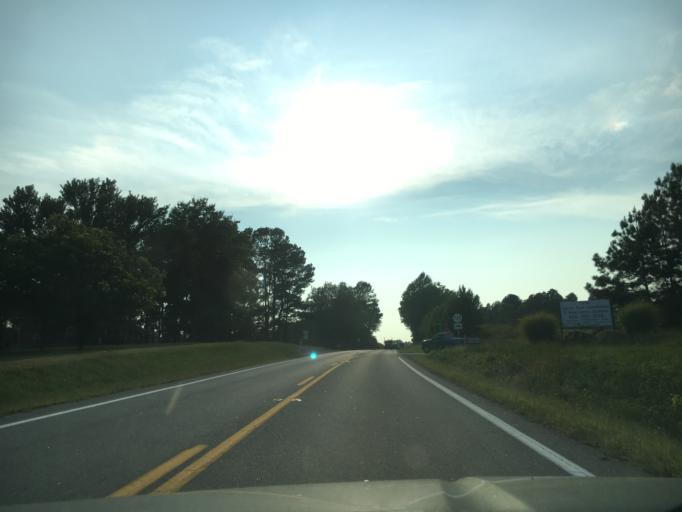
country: US
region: Virginia
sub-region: Prince Edward County
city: Farmville
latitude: 37.2731
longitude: -78.2813
